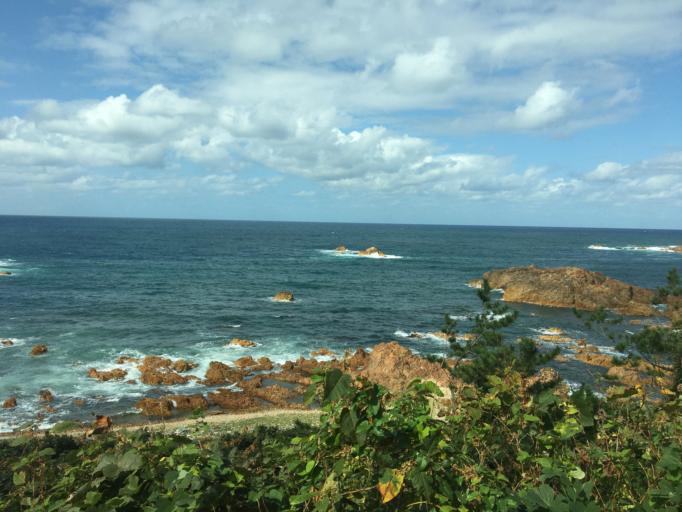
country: JP
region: Aomori
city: Shimokizukuri
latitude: 40.6647
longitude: 139.9395
